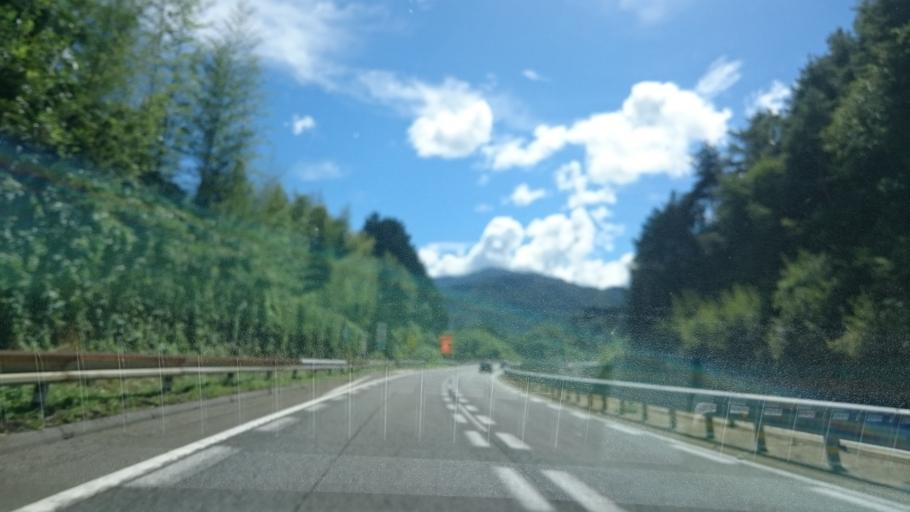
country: JP
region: Nagano
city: Iida
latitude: 35.4527
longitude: 137.7496
